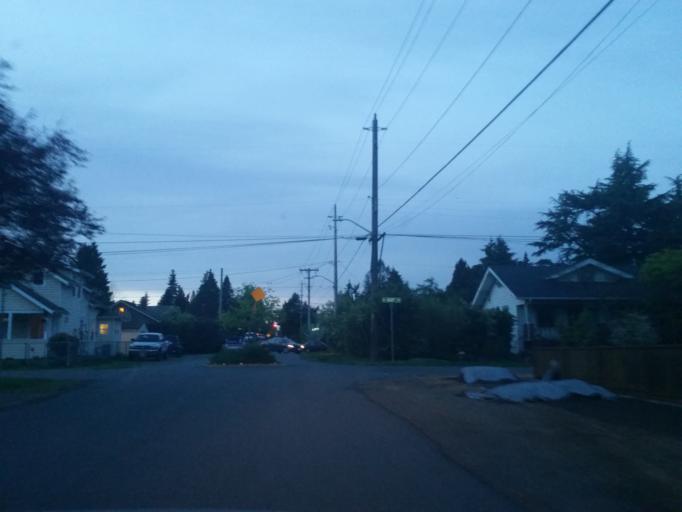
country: US
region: Washington
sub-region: King County
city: Shoreline
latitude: 47.7026
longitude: -122.3528
